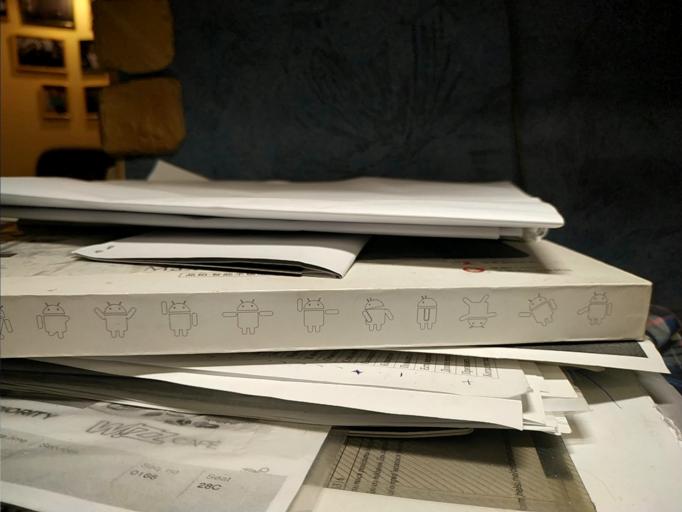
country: RU
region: Tverskaya
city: Zubtsov
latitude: 56.0813
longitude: 34.7964
